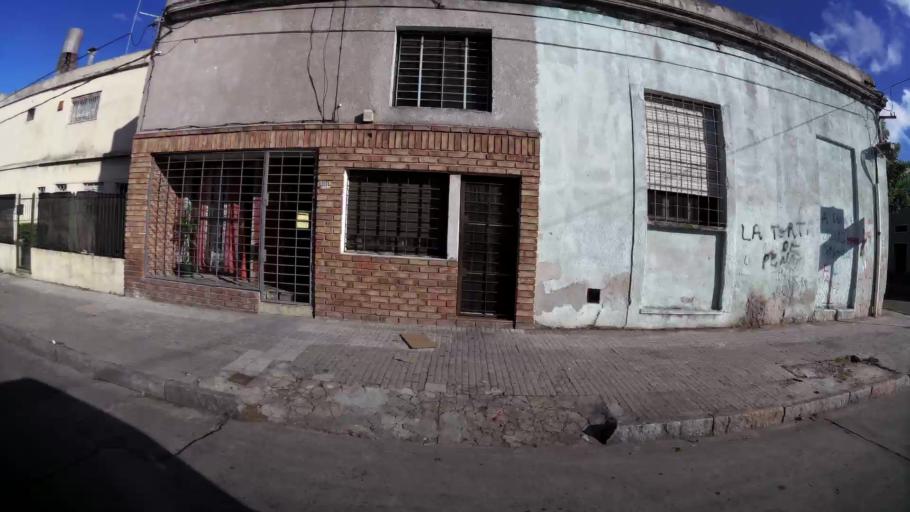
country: UY
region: Montevideo
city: Montevideo
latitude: -34.8712
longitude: -56.1378
